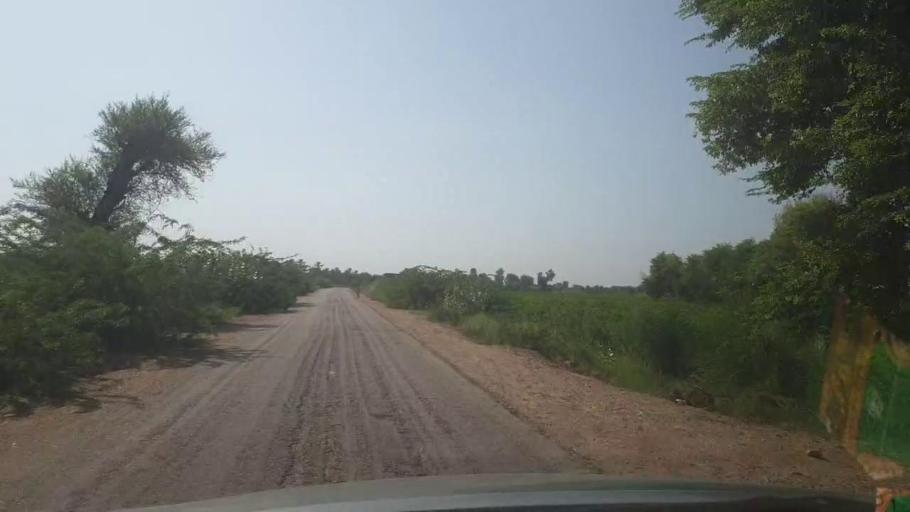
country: PK
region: Sindh
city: Rohri
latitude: 27.4709
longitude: 69.0344
